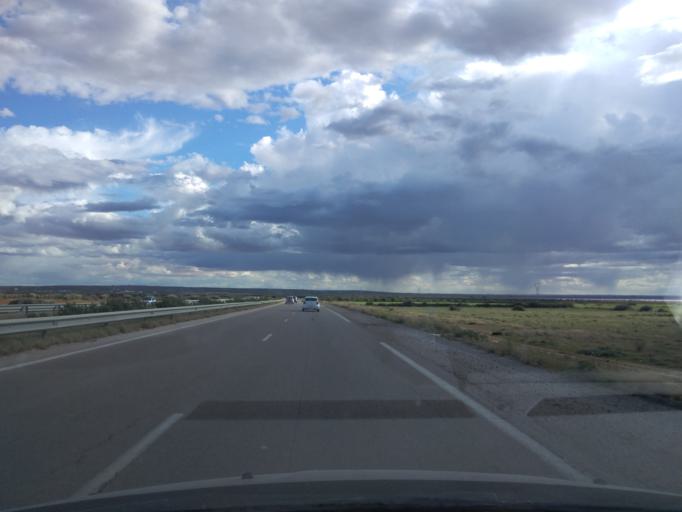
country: TN
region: Al Munastir
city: Manzil Kamil
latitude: 35.5034
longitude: 10.6252
